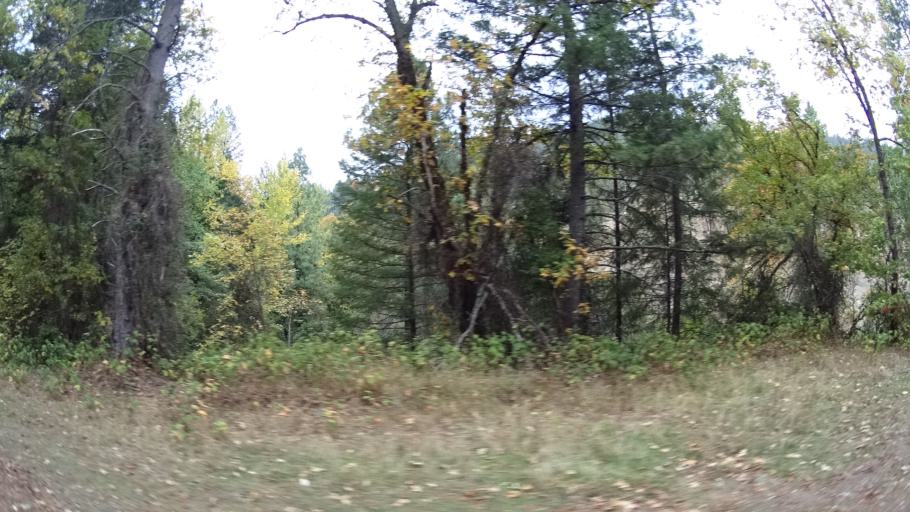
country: US
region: California
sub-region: Siskiyou County
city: Happy Camp
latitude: 41.7817
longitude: -123.3223
